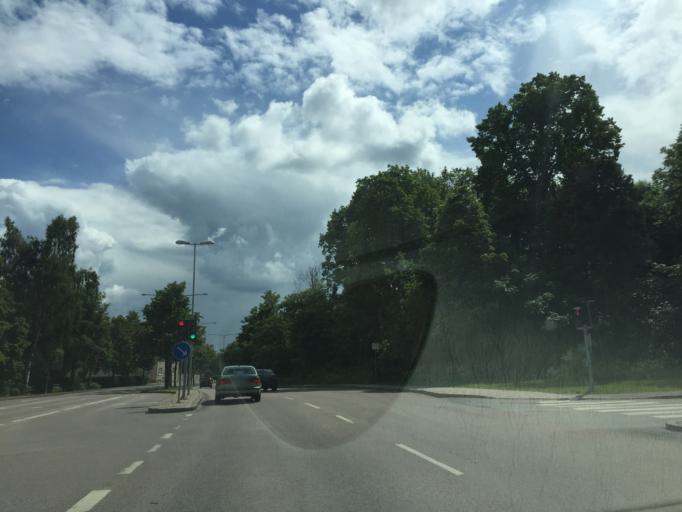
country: SE
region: Vaestmanland
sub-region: Vasteras
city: Vasteras
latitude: 59.6073
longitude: 16.5399
